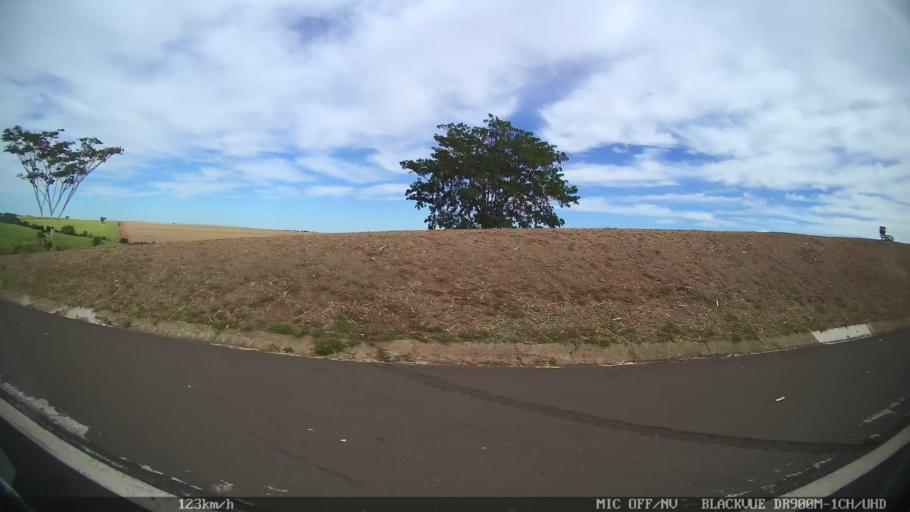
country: BR
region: Sao Paulo
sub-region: Pindorama
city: Pindorama
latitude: -21.1941
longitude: -48.9472
